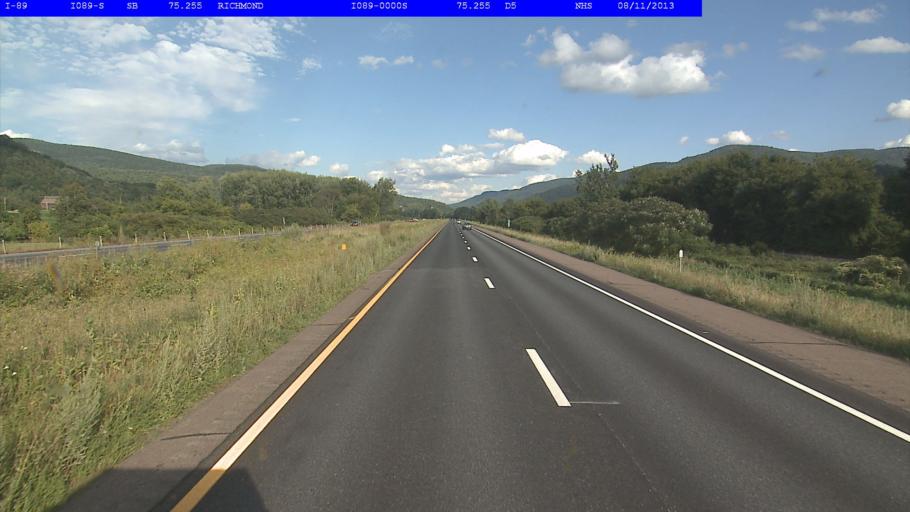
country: US
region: Vermont
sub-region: Chittenden County
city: Williston
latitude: 44.3949
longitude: -72.9667
